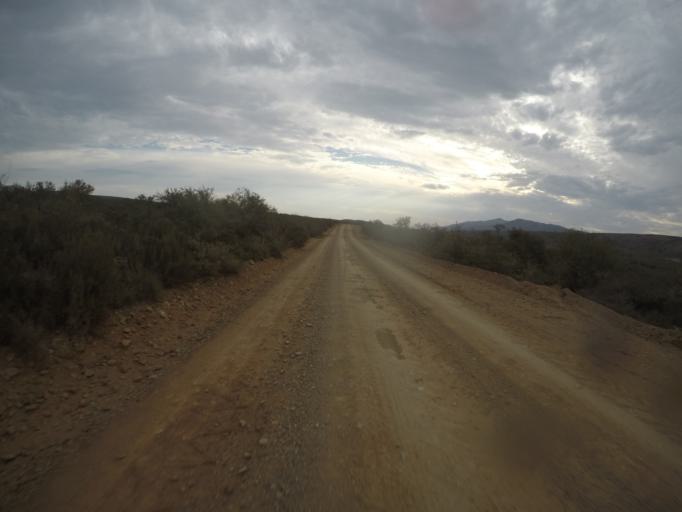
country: ZA
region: Eastern Cape
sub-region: Cacadu District Municipality
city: Willowmore
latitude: -33.4923
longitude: 23.5824
